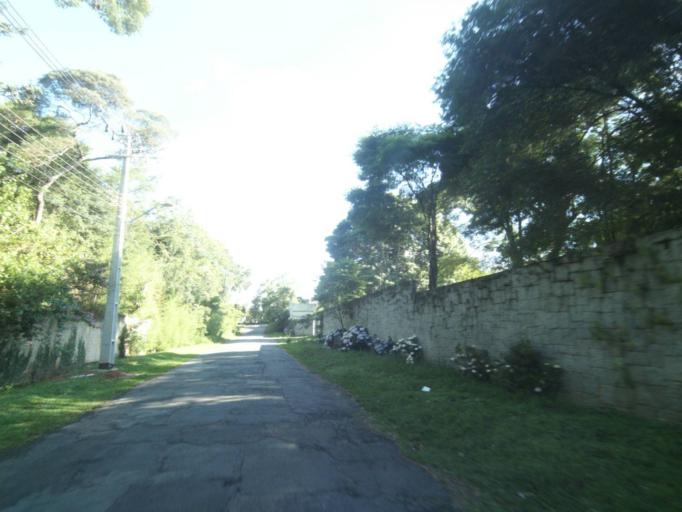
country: BR
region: Parana
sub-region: Curitiba
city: Curitiba
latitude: -25.4507
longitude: -49.3185
